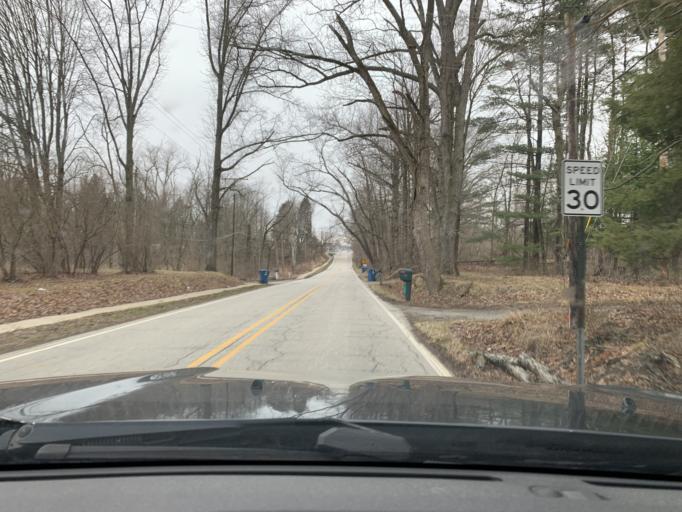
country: US
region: Indiana
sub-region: Porter County
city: Chesterton
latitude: 41.6170
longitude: -87.0310
